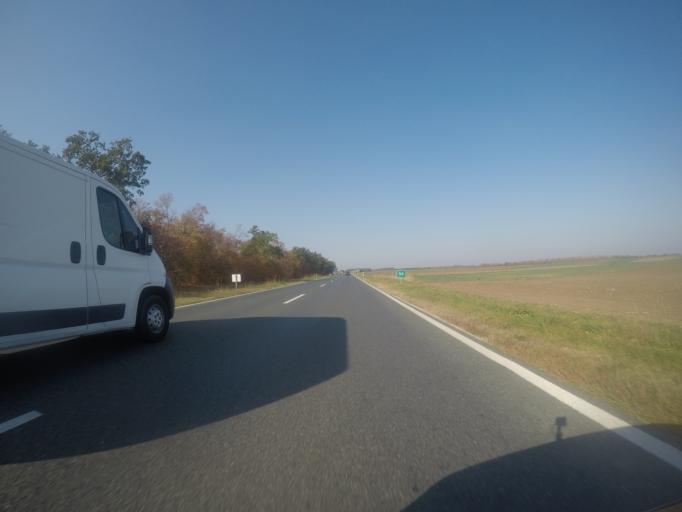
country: HU
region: Tolna
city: Madocsa
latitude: 46.7214
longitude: 18.8851
